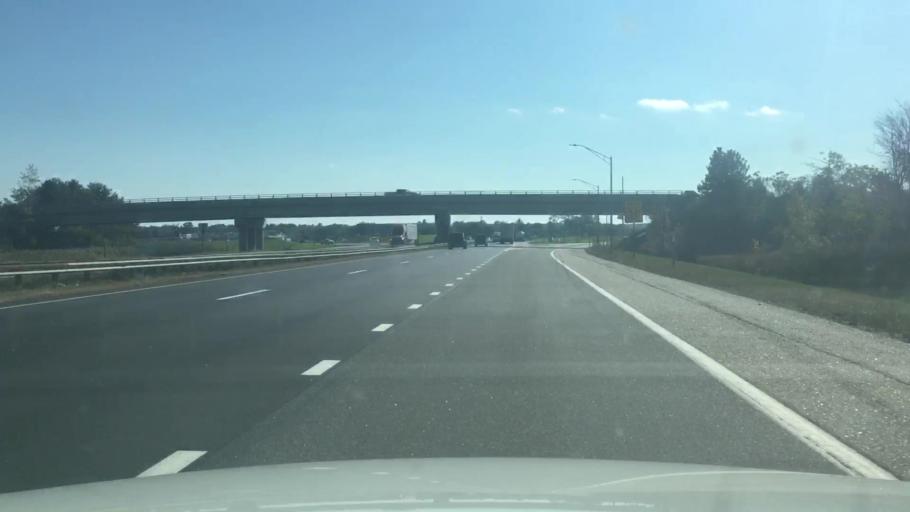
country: US
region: Maine
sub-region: Cumberland County
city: South Portland Gardens
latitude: 43.6507
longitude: -70.3314
